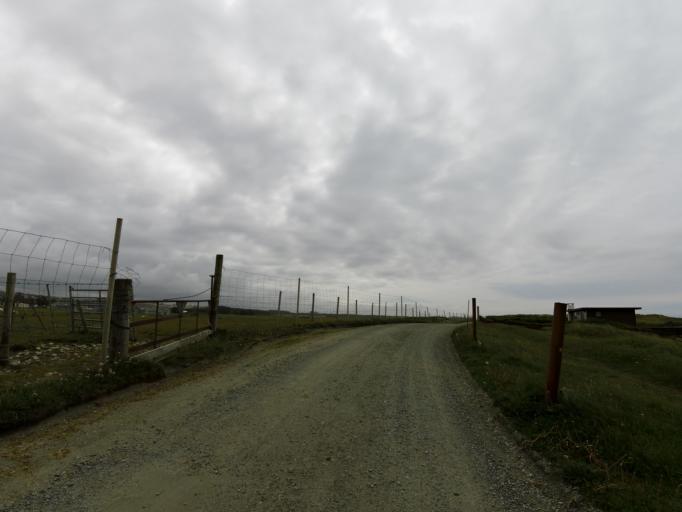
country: NO
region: Rogaland
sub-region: Klepp
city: Kleppe
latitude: 58.8018
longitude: 5.5521
